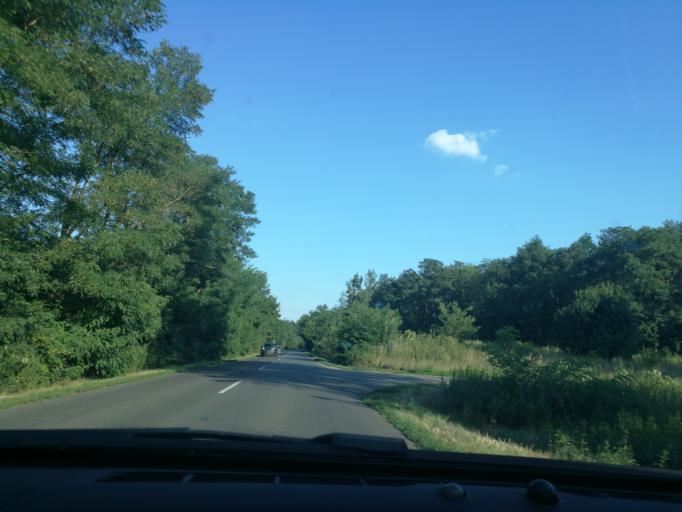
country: HU
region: Szabolcs-Szatmar-Bereg
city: Tiszabercel
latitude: 48.1468
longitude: 21.6247
